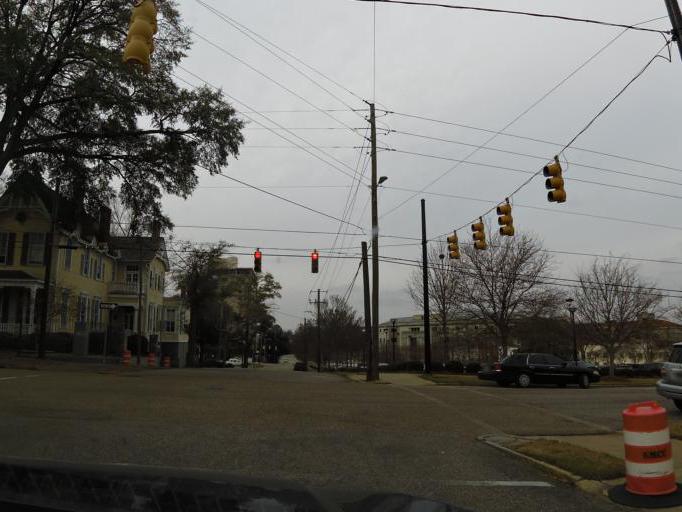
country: US
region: Alabama
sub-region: Montgomery County
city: Montgomery
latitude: 32.3736
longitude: -86.3071
